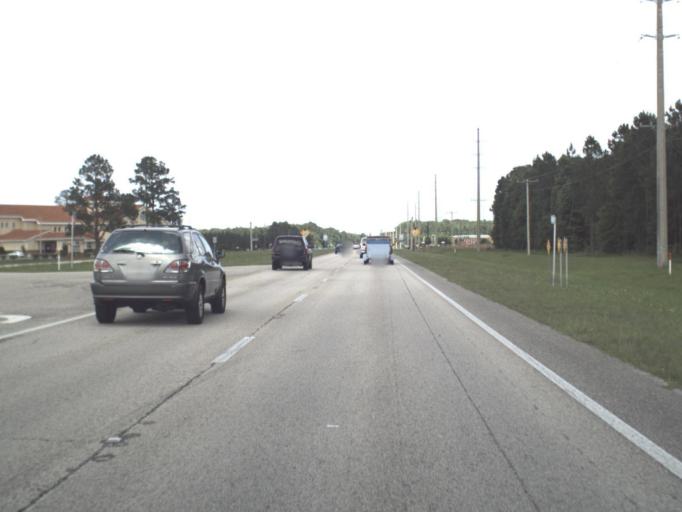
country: US
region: Florida
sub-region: Clay County
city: Lakeside
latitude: 30.1121
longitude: -81.8165
